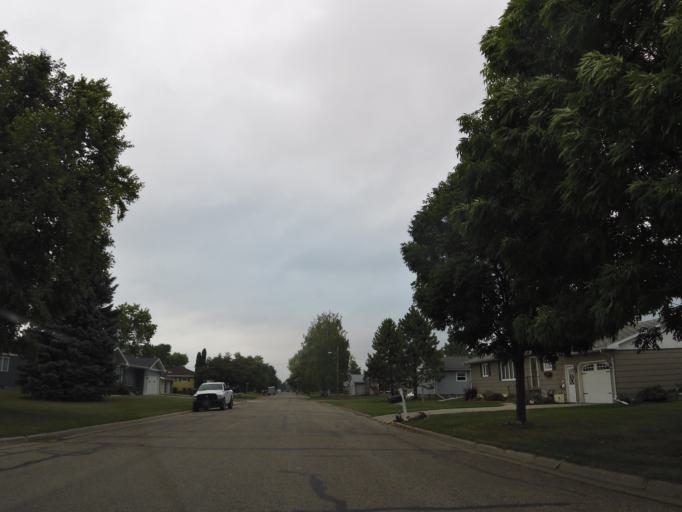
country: US
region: North Dakota
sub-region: Walsh County
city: Grafton
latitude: 48.5573
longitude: -97.1833
